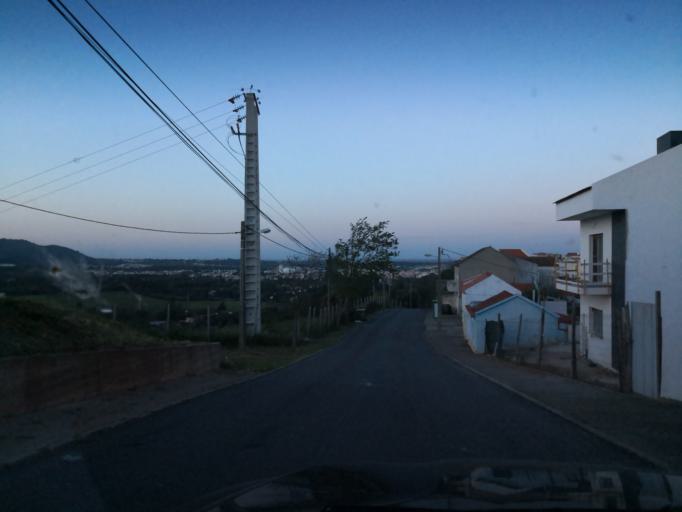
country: PT
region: Setubal
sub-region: Setubal
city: Setubal
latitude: 38.5279
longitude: -8.9112
